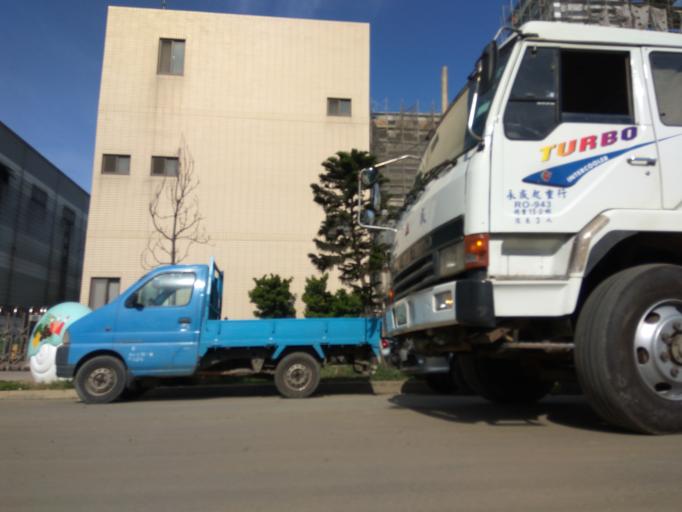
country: TW
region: Taiwan
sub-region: Hsinchu
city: Zhubei
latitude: 25.0362
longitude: 121.0588
